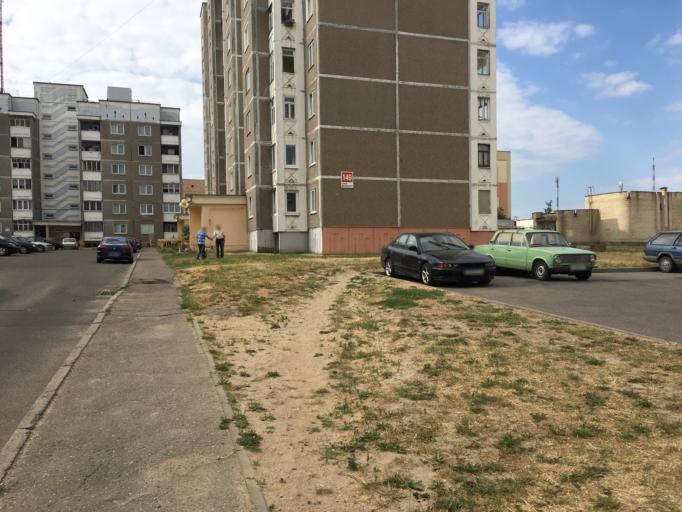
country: BY
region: Grodnenskaya
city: Hrodna
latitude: 53.7134
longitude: 23.8422
